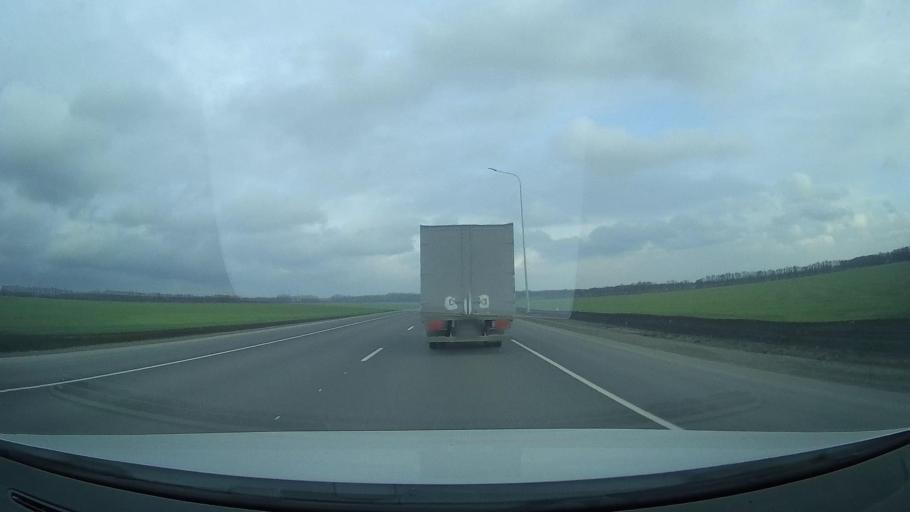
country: RU
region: Rostov
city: Grushevskaya
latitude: 47.4673
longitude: 39.8971
